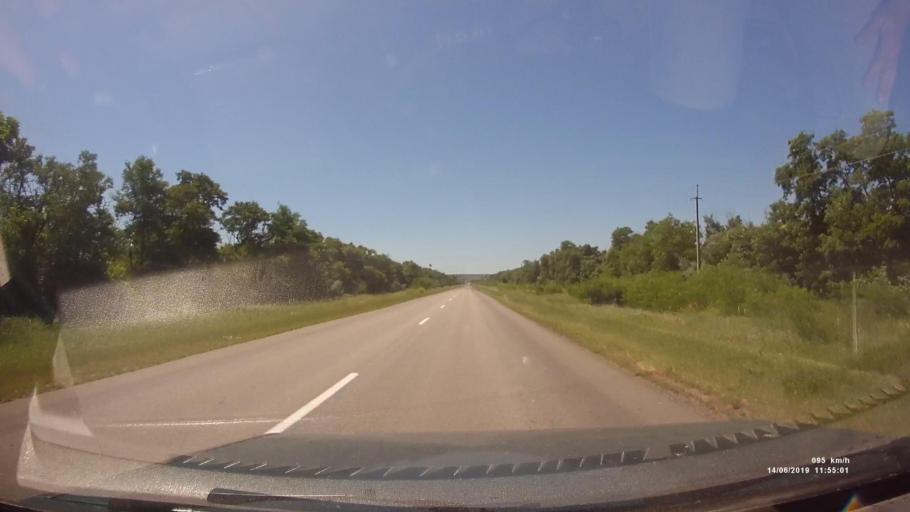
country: RU
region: Rostov
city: Kazanskaya
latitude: 49.8140
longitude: 41.1842
